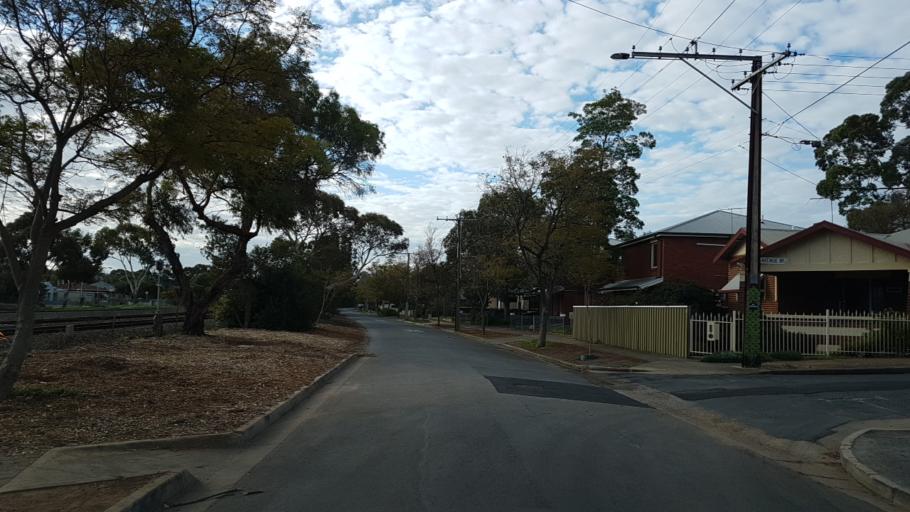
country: AU
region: South Australia
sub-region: Adelaide
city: North Adelaide
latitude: -34.8955
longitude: 138.5844
